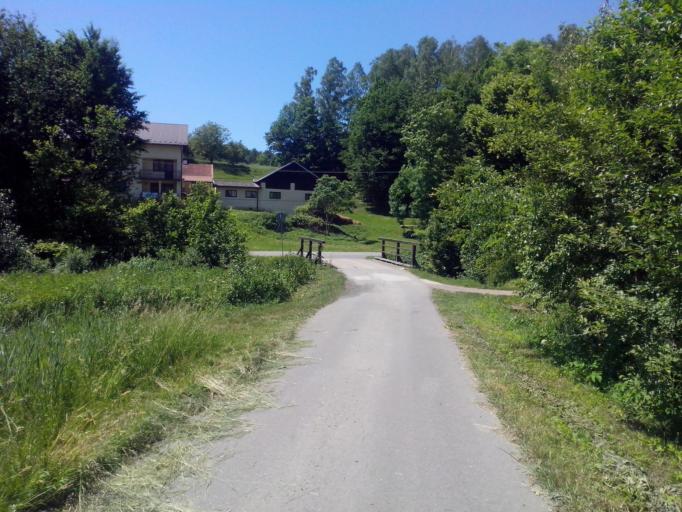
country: PL
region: Subcarpathian Voivodeship
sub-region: Powiat krosnienski
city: Leki
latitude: 49.8159
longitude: 21.6757
